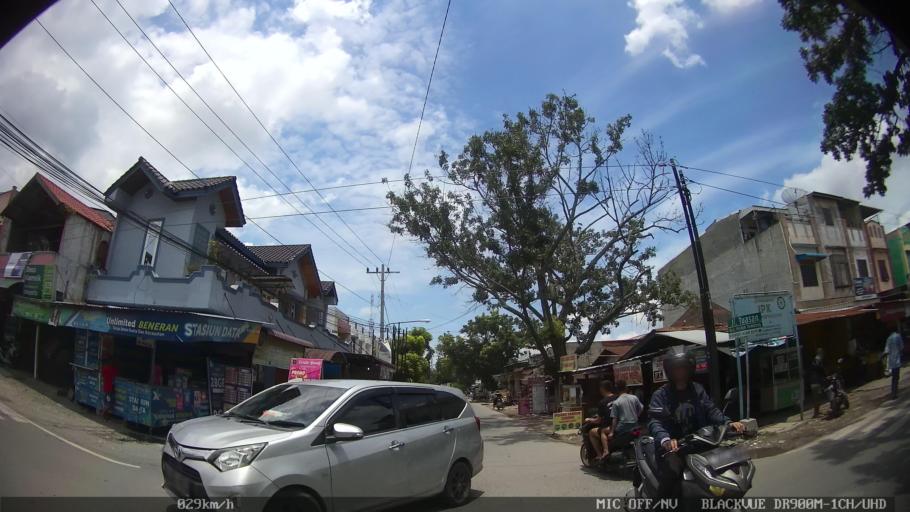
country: ID
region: North Sumatra
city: Medan
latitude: 3.6160
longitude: 98.6965
